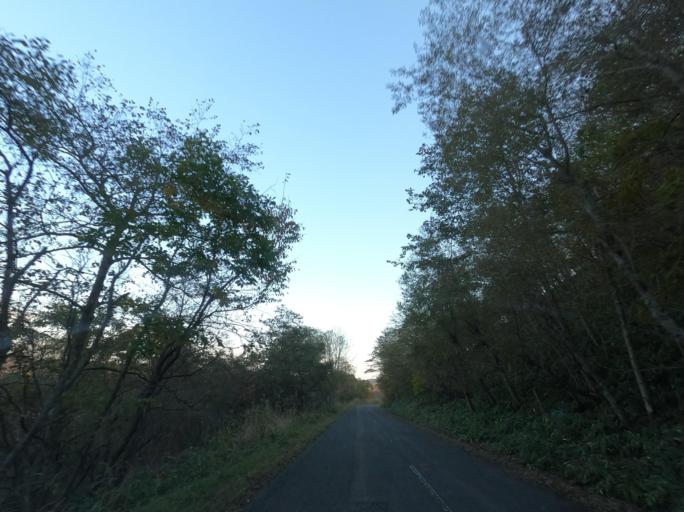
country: JP
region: Hokkaido
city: Kushiro
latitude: 43.1926
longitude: 144.4652
